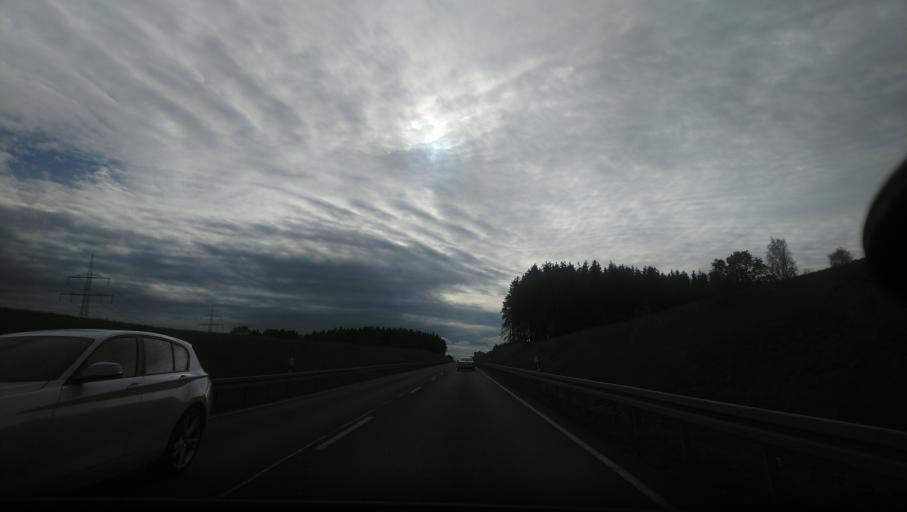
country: DE
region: Saxony
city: Dorfchemnitz
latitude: 50.6798
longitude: 12.8040
